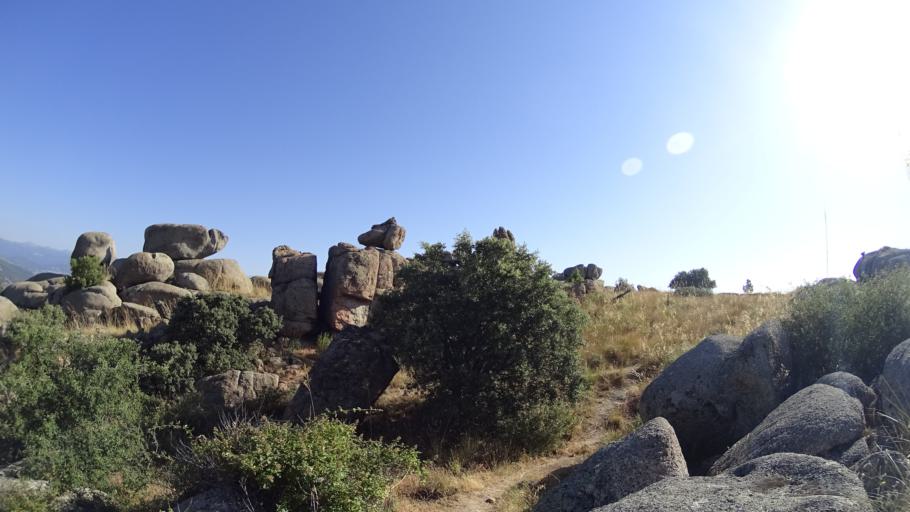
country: ES
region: Madrid
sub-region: Provincia de Madrid
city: Moralzarzal
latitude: 40.6512
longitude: -3.9487
